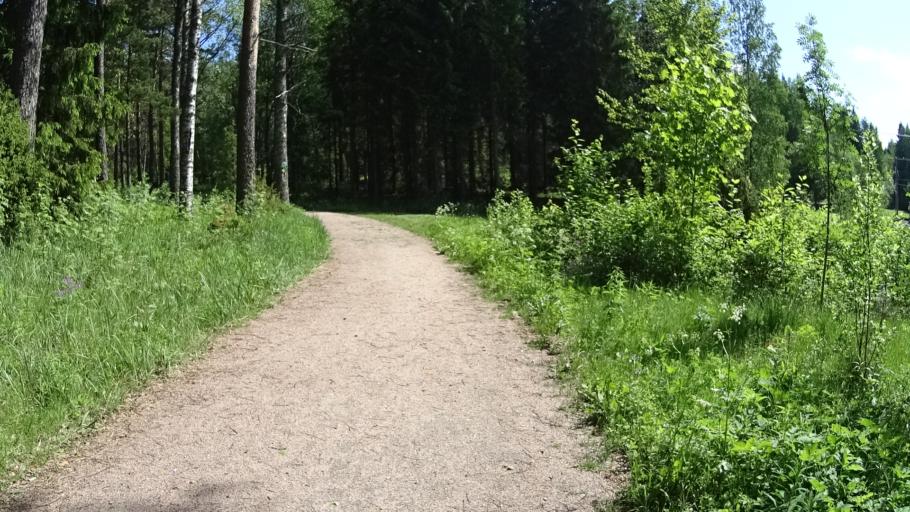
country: FI
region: Uusimaa
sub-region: Helsinki
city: Kauniainen
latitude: 60.3146
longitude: 24.6839
